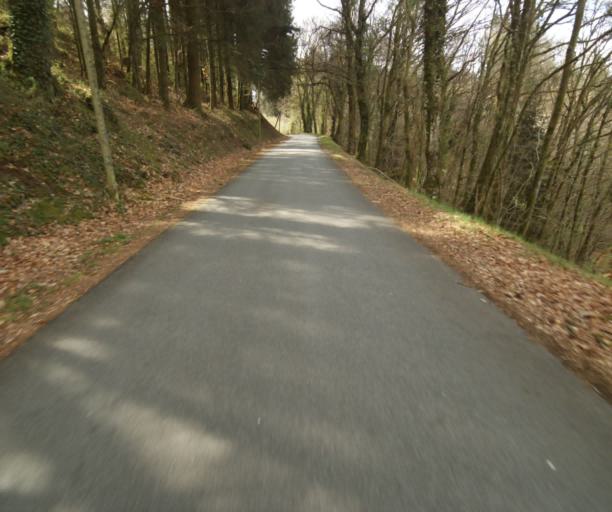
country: FR
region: Limousin
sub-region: Departement de la Correze
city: Correze
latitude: 45.3712
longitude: 1.8811
